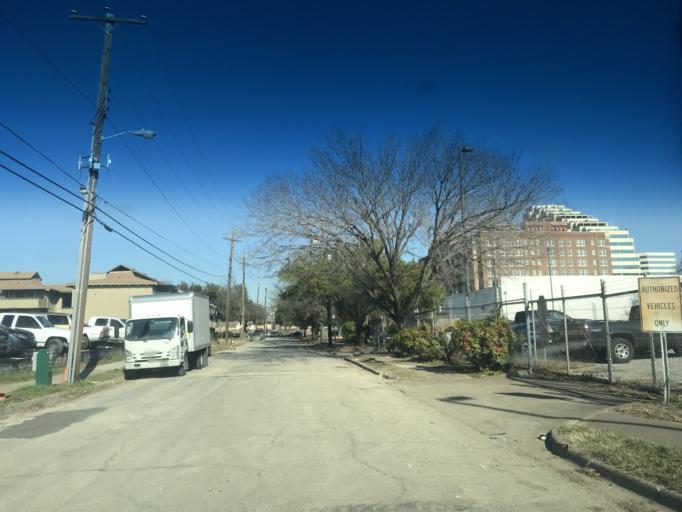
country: US
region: Texas
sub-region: Dallas County
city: Dallas
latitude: 32.8086
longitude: -96.8114
